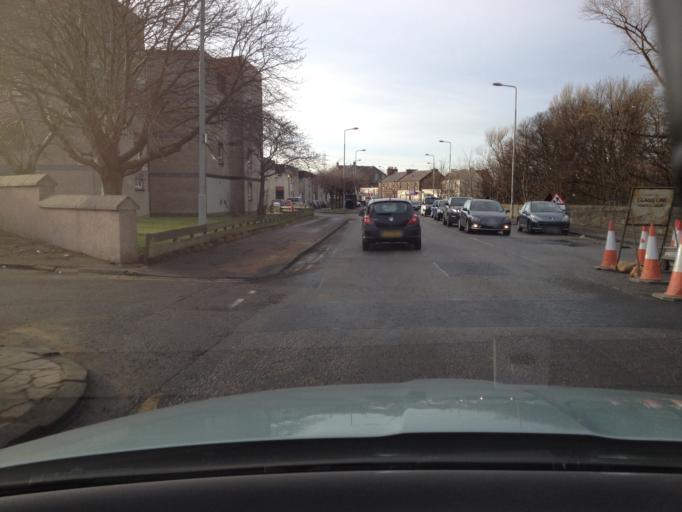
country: GB
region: Scotland
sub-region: Edinburgh
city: Colinton
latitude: 55.9251
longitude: -3.2566
